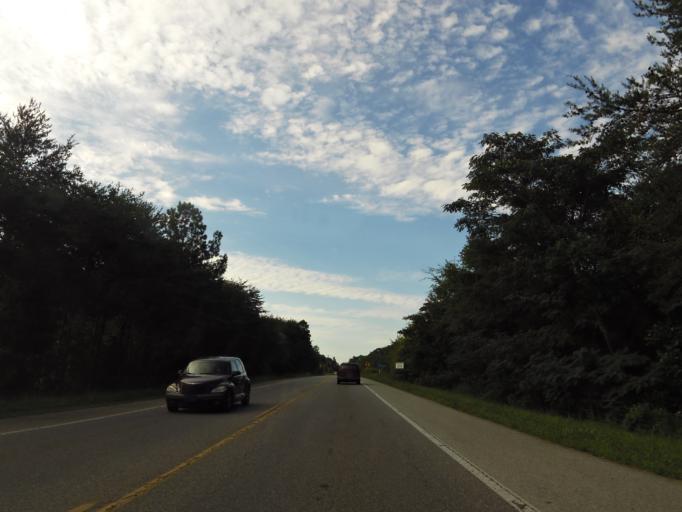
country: US
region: Tennessee
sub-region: Monroe County
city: Vonore
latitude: 35.5879
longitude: -84.2737
